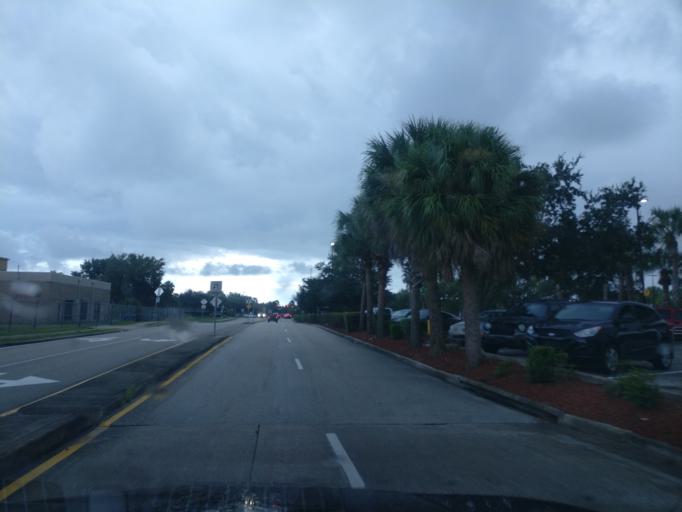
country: US
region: Florida
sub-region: Brevard County
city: South Patrick Shores
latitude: 28.2327
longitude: -80.7228
